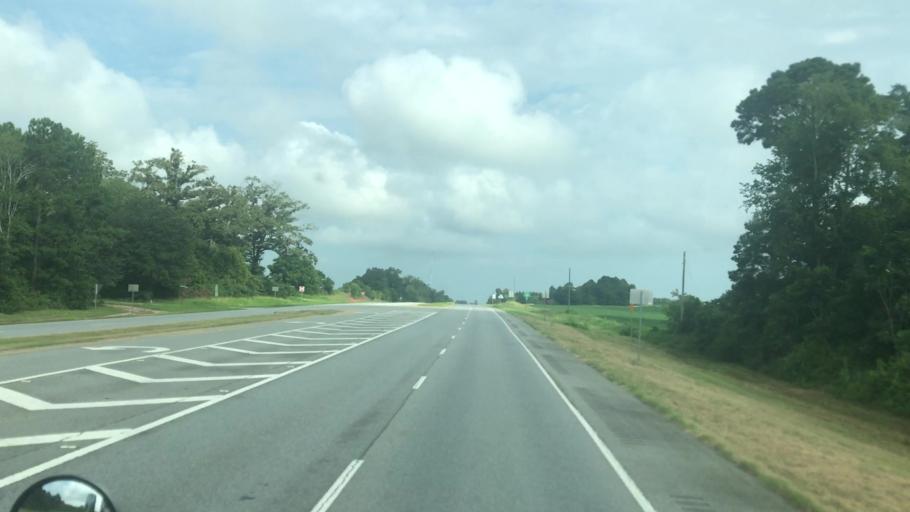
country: US
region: Georgia
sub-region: Miller County
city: Colquitt
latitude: 31.2531
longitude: -84.8017
